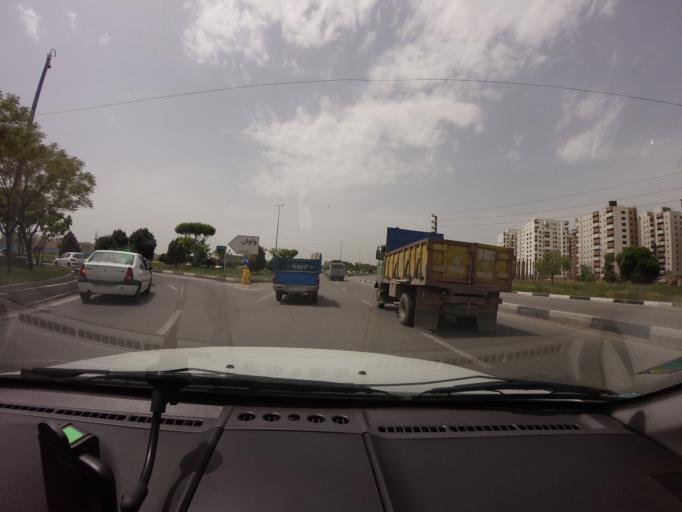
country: IR
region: Tehran
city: Eslamshahr
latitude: 35.5173
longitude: 51.2254
